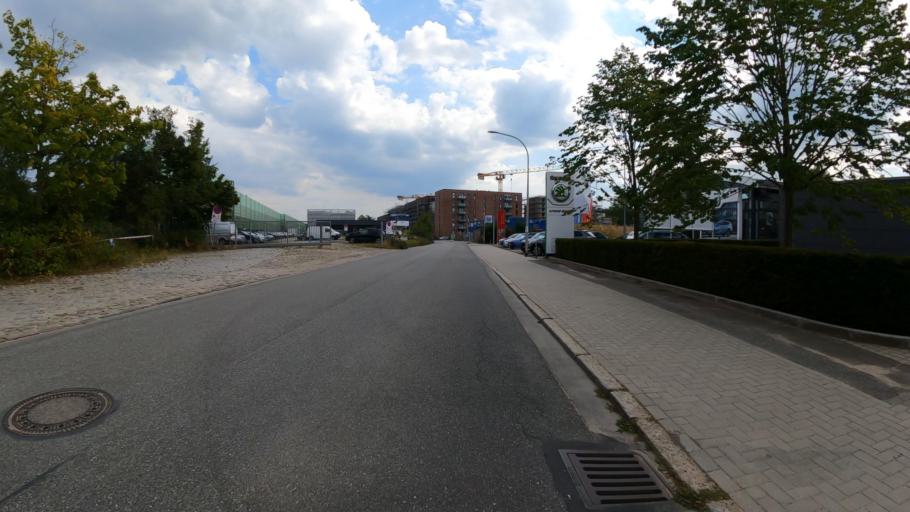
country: DE
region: Schleswig-Holstein
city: Pinneberg
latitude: 53.6579
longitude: 9.7929
